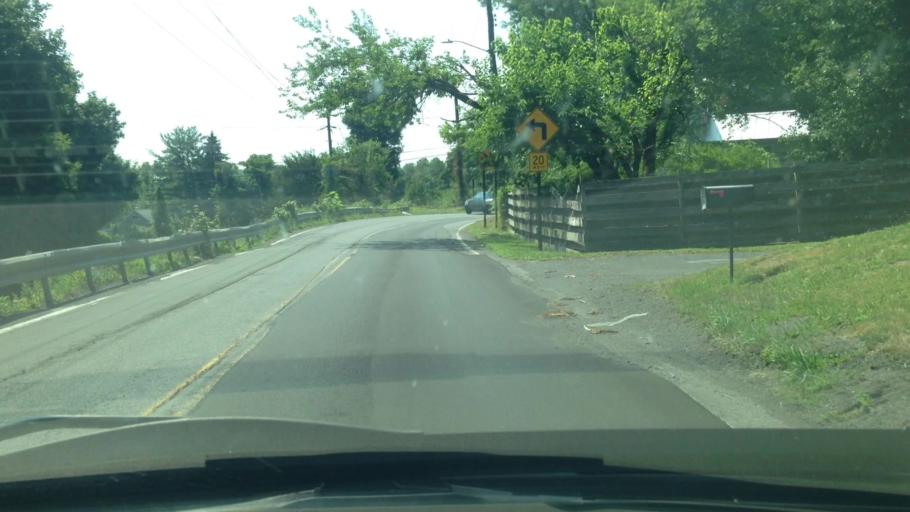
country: US
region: New York
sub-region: Ulster County
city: Port Ewen
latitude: 41.9000
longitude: -73.9897
